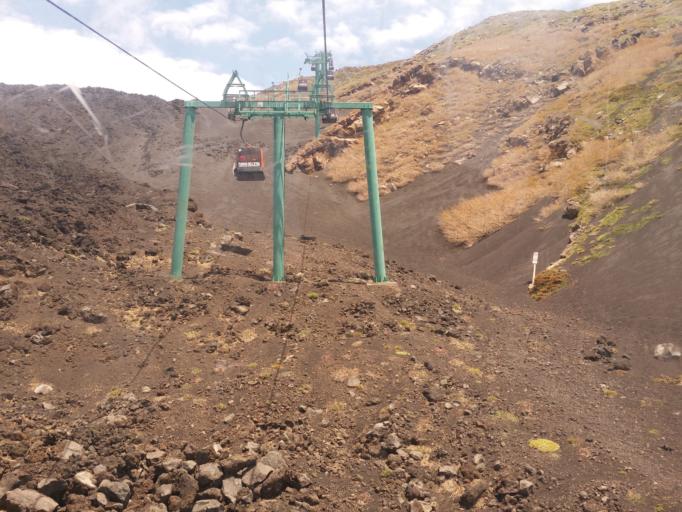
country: IT
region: Sicily
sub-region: Catania
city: Ragalna
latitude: 37.7106
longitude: 14.9995
